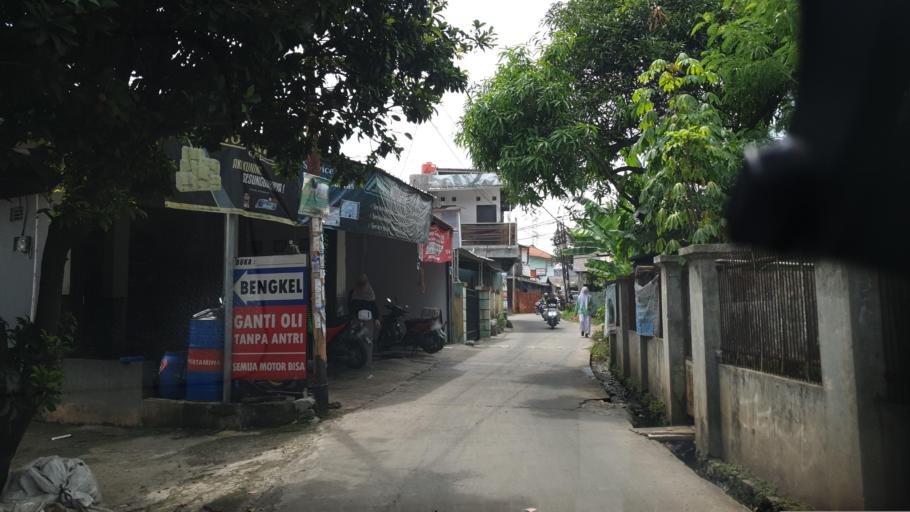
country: ID
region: West Java
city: Sawangan
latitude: -6.3761
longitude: 106.7601
